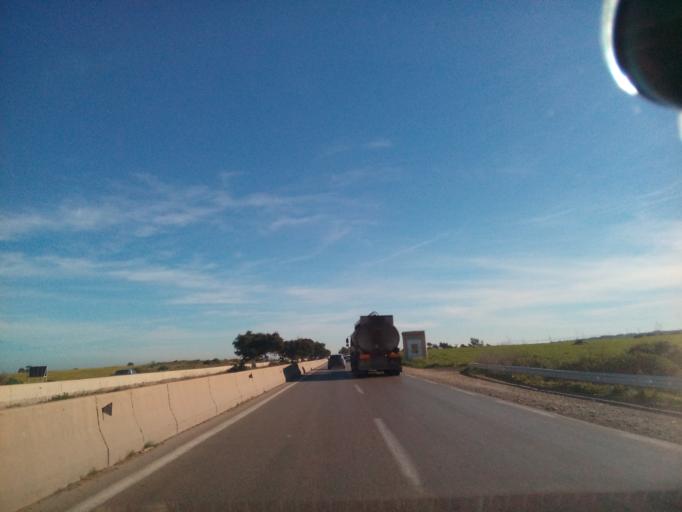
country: DZ
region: Oran
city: Ain el Bya
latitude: 35.7669
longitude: -0.2171
